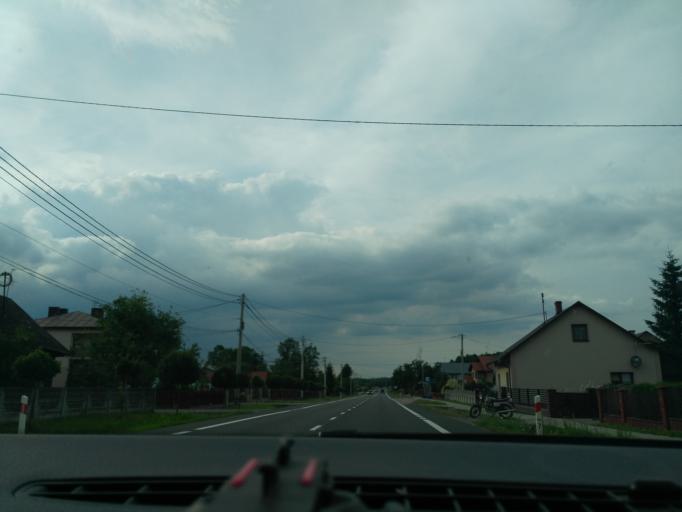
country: PL
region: Subcarpathian Voivodeship
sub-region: Powiat rzeszowski
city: Kamien
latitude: 50.3528
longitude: 22.1249
